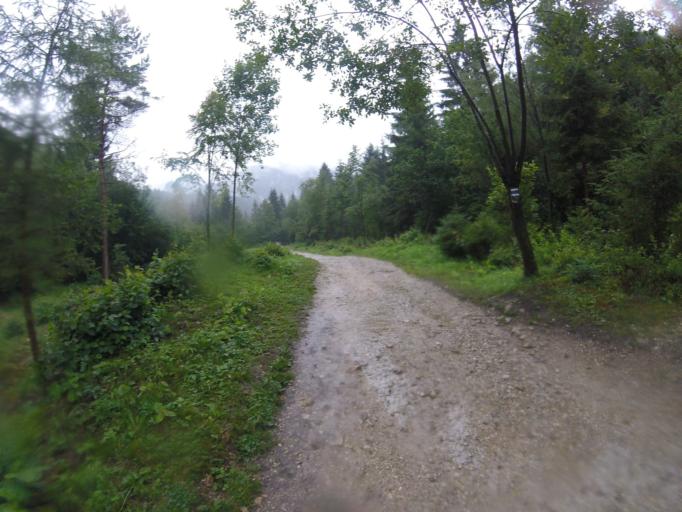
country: SK
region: Zilinsky
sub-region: Okres Zilina
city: Terchova
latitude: 49.2556
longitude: 19.0679
